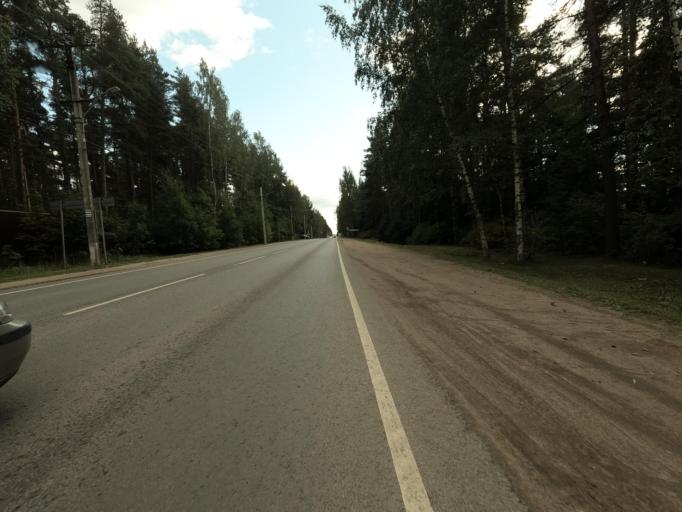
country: RU
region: Leningrad
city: Vsevolozhsk
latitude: 60.0048
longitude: 30.6636
